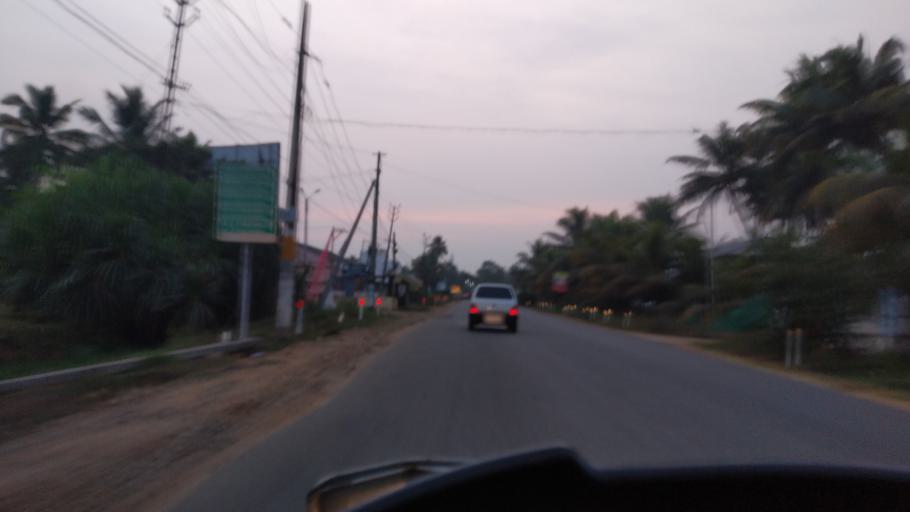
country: IN
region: Kerala
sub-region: Kottayam
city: Kottayam
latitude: 9.5921
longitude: 76.4428
